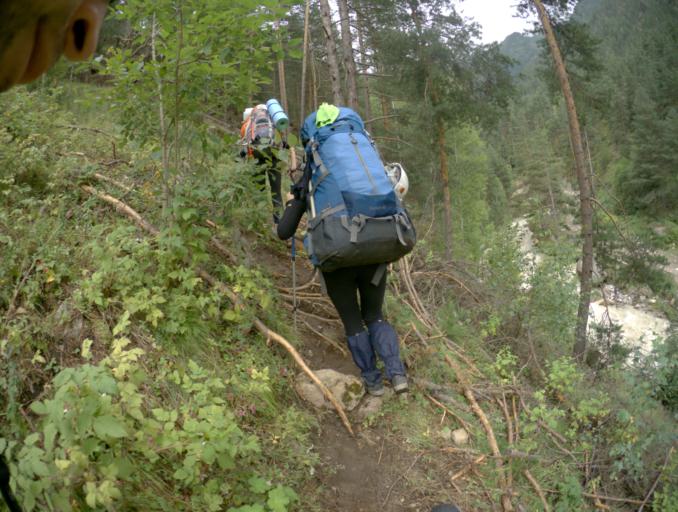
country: RU
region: Karachayevo-Cherkesiya
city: Uchkulan
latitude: 43.4219
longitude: 42.2032
